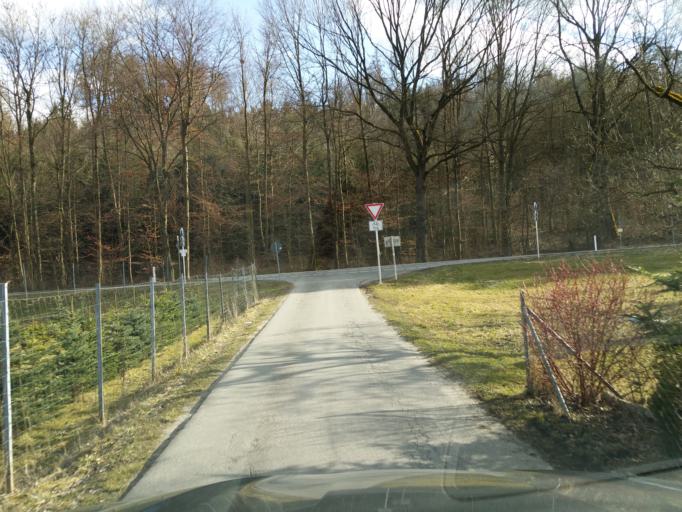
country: DE
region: Bavaria
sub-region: Lower Bavaria
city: Eching
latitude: 48.4970
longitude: 12.0491
